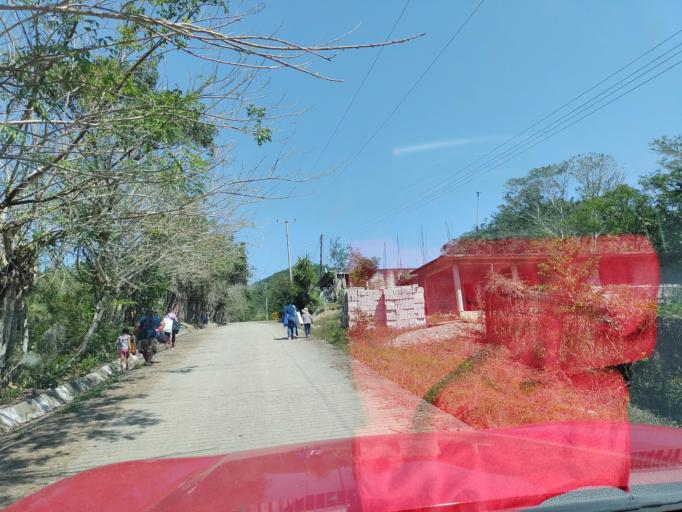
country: MX
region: Veracruz
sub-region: Papantla
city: Polutla
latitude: 20.5021
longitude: -97.2140
